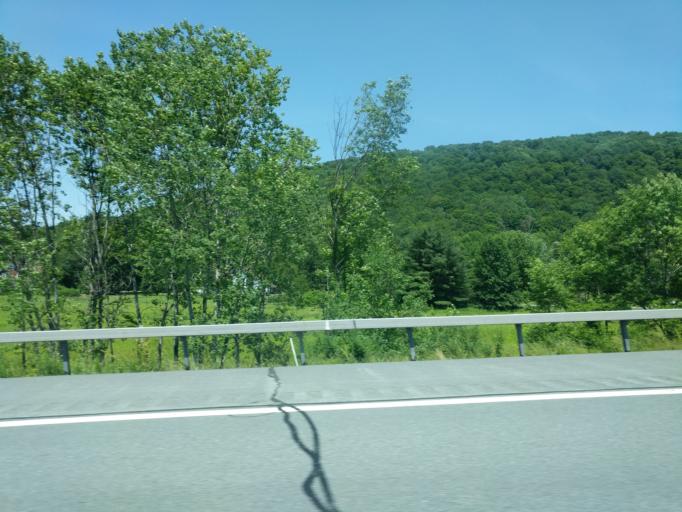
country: US
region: New York
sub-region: Sullivan County
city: Livingston Manor
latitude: 41.9126
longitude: -74.8329
